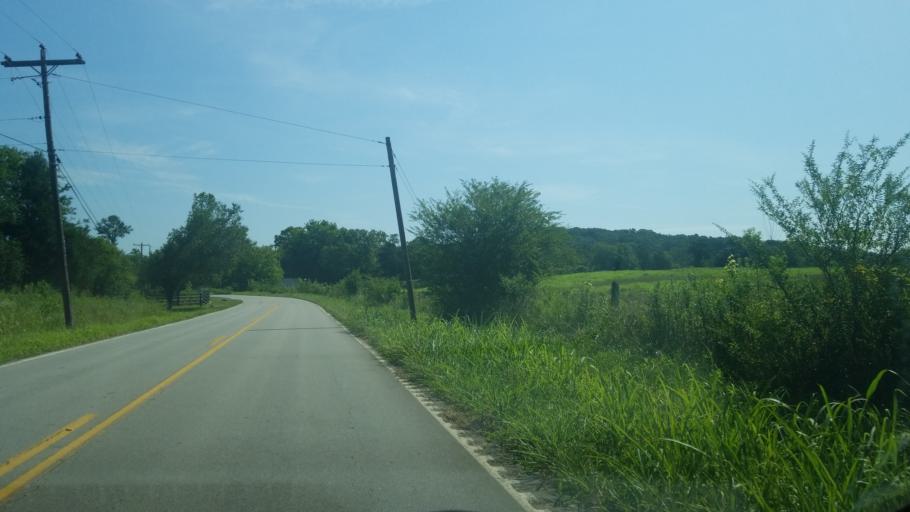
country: US
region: Tennessee
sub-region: Hamilton County
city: Sale Creek
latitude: 35.3331
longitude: -85.0084
